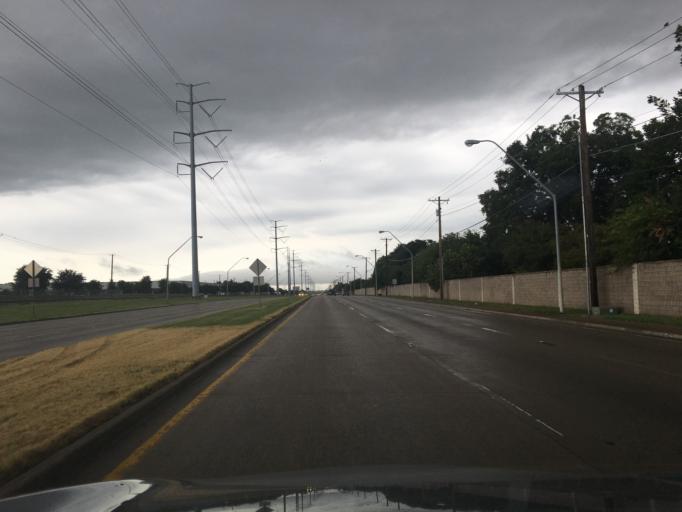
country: US
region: Texas
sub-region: Dallas County
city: Garland
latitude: 32.9320
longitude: -96.6253
